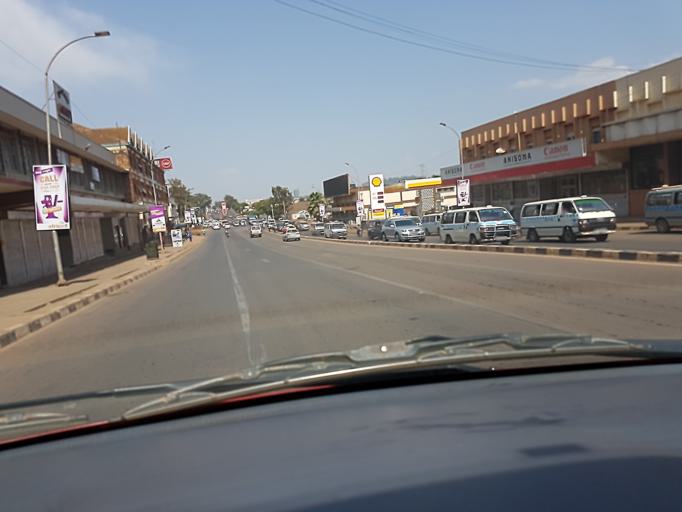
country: UG
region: Central Region
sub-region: Kampala District
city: Kampala
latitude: 0.3159
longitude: 32.5921
